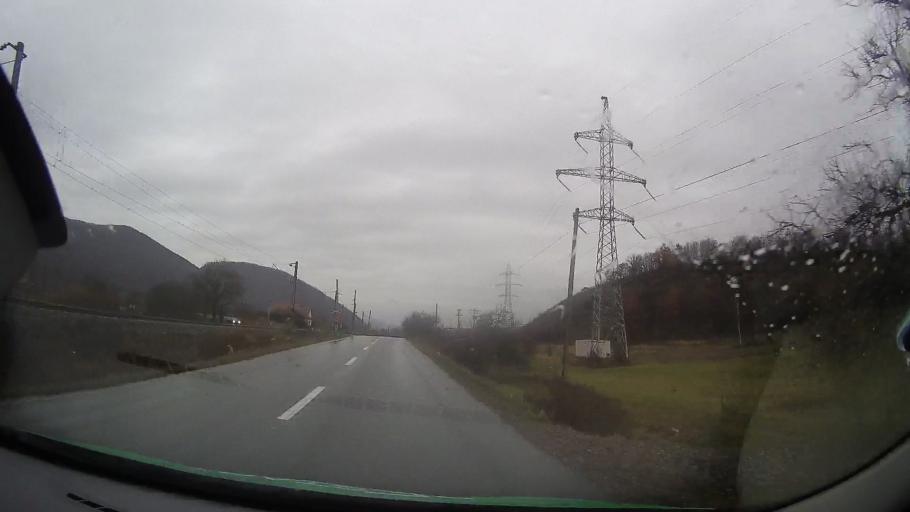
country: RO
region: Bistrita-Nasaud
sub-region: Municipiul Bistrita
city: Viisoara
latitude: 47.0501
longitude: 24.4541
